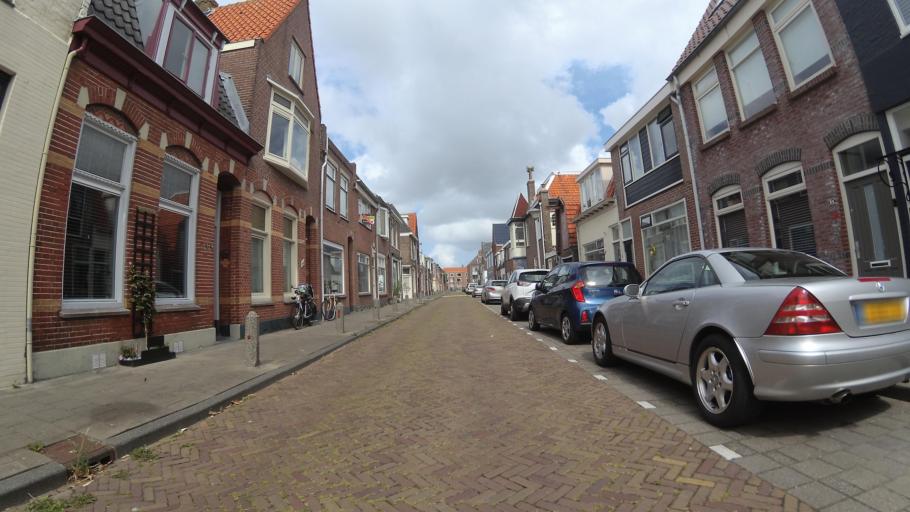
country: NL
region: North Holland
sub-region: Gemeente Den Helder
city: Den Helder
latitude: 52.9609
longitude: 4.7564
